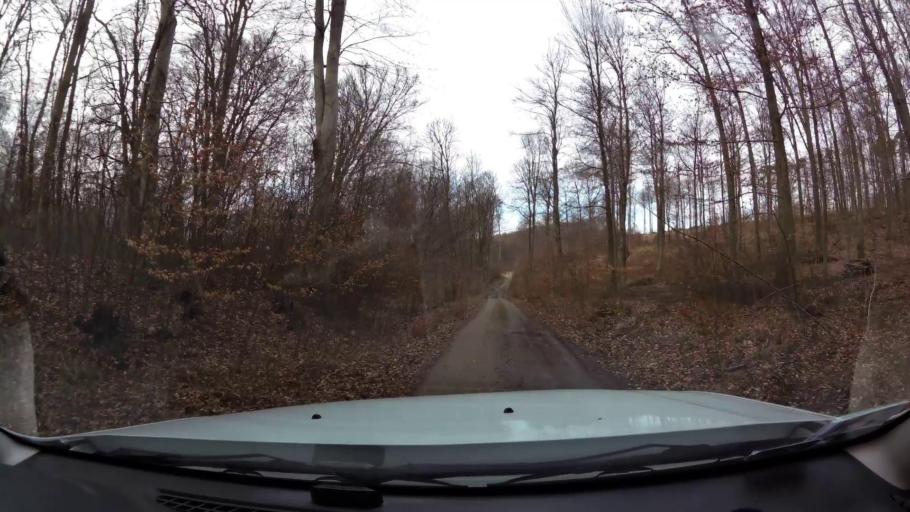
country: PL
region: West Pomeranian Voivodeship
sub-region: Powiat drawski
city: Drawsko Pomorskie
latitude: 53.4997
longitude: 15.7107
